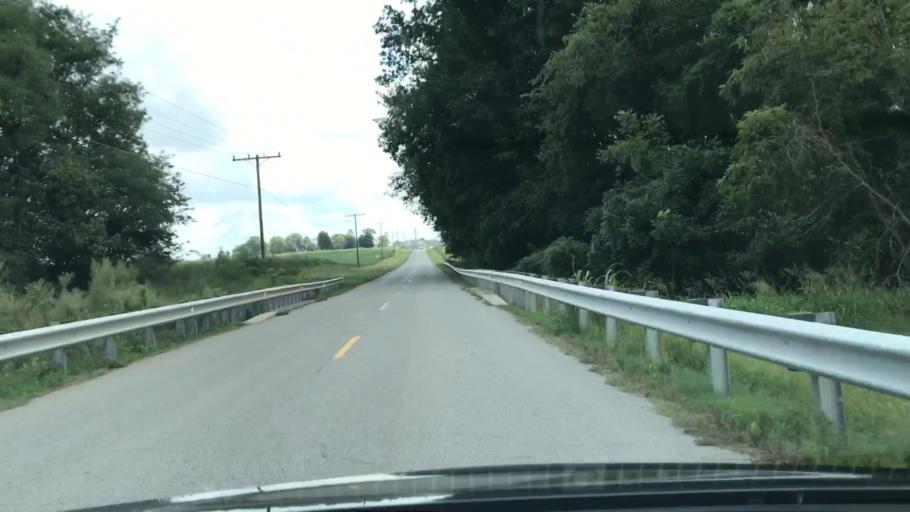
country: US
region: Kentucky
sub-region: Todd County
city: Guthrie
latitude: 36.7224
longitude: -87.0822
